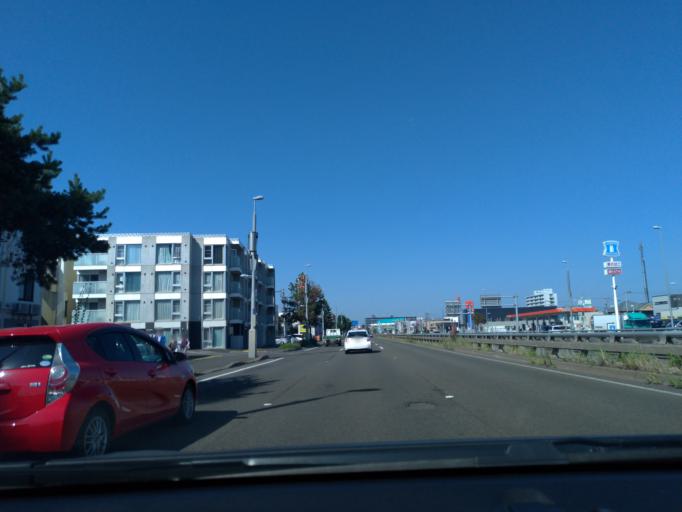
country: JP
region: Hokkaido
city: Sapporo
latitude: 43.1030
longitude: 141.3447
